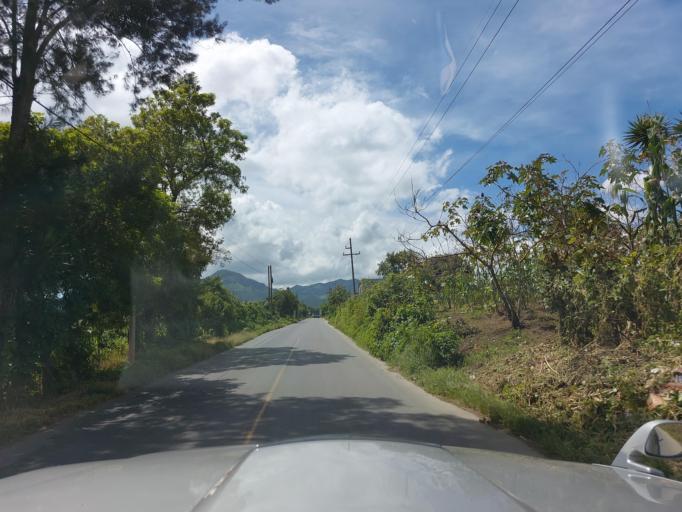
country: GT
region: Chimaltenango
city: Parramos
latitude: 14.6138
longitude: -90.8206
